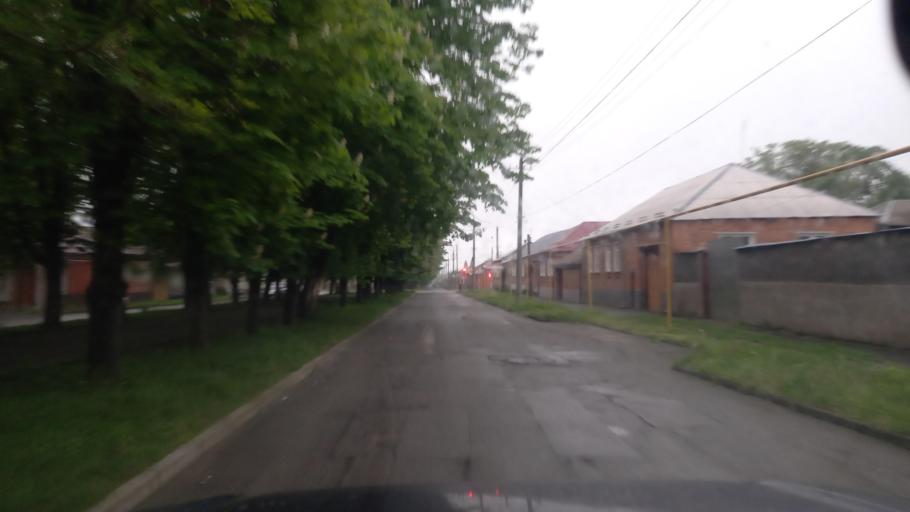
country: RU
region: North Ossetia
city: Alagir
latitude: 43.0413
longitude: 44.2202
